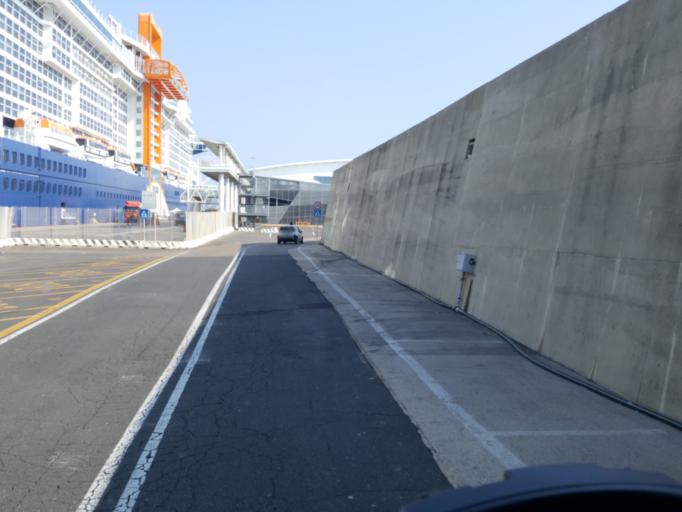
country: IT
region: Latium
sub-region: Citta metropolitana di Roma Capitale
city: Civitavecchia
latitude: 42.0969
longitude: 11.7762
